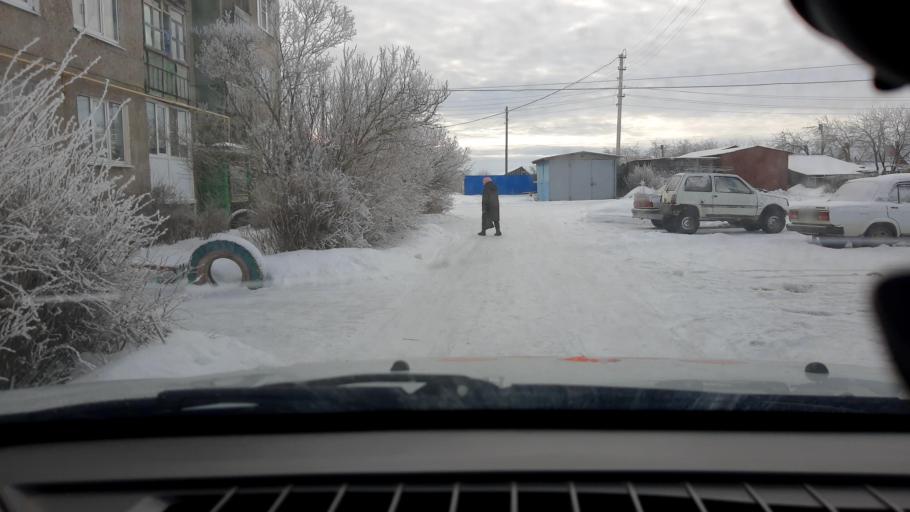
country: RU
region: Nizjnij Novgorod
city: Bogorodsk
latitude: 56.0358
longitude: 43.6221
